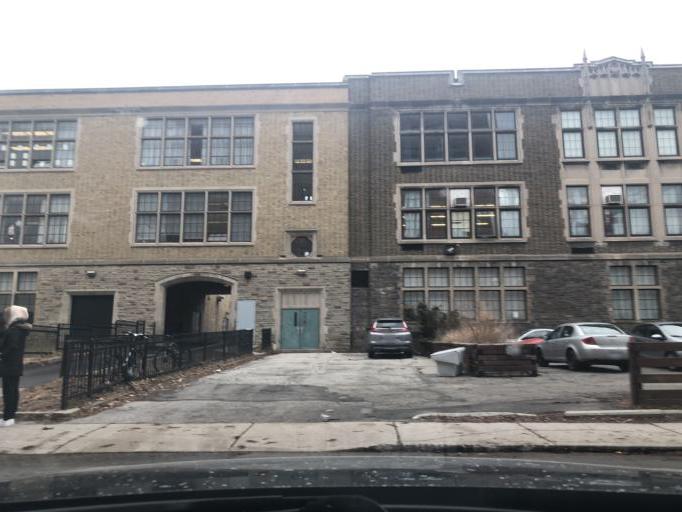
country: CA
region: Ontario
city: Toronto
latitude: 43.6819
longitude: -79.3342
